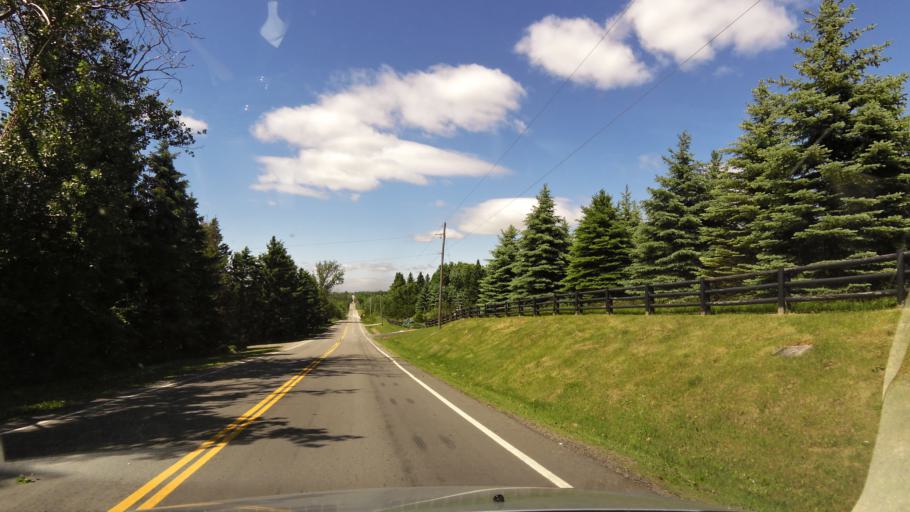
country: CA
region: Ontario
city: Newmarket
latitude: 43.9924
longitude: -79.5454
